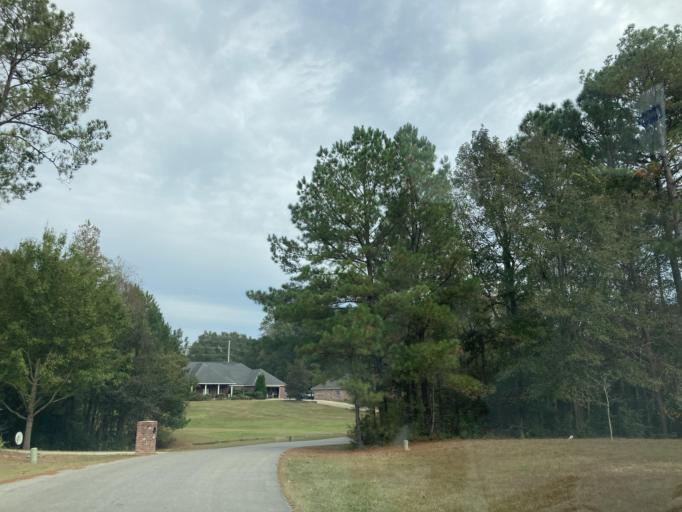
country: US
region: Mississippi
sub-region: Lamar County
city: Arnold Line
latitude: 31.3366
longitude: -89.4065
